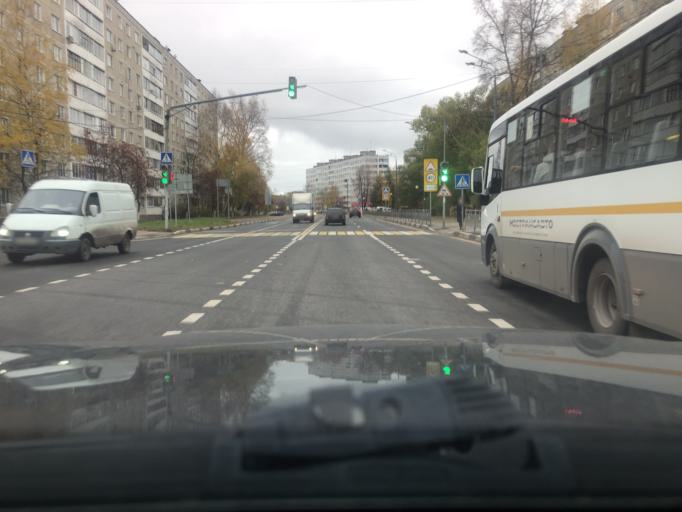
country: RU
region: Moskovskaya
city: Sergiyev Posad
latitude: 56.3247
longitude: 38.1341
